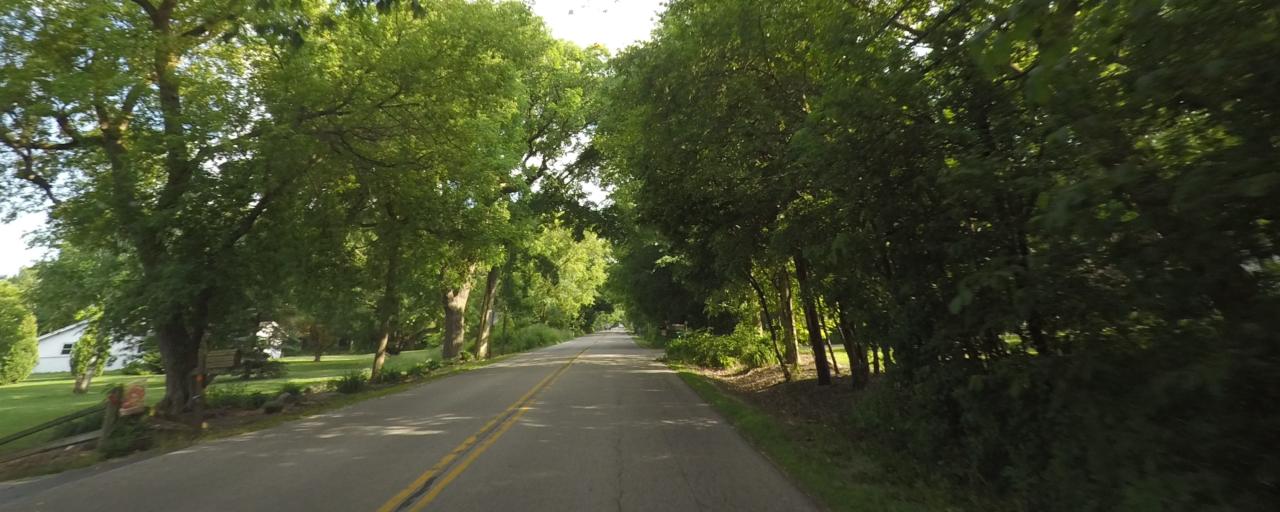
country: US
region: Wisconsin
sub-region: Milwaukee County
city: Hales Corners
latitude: 42.9405
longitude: -88.0285
